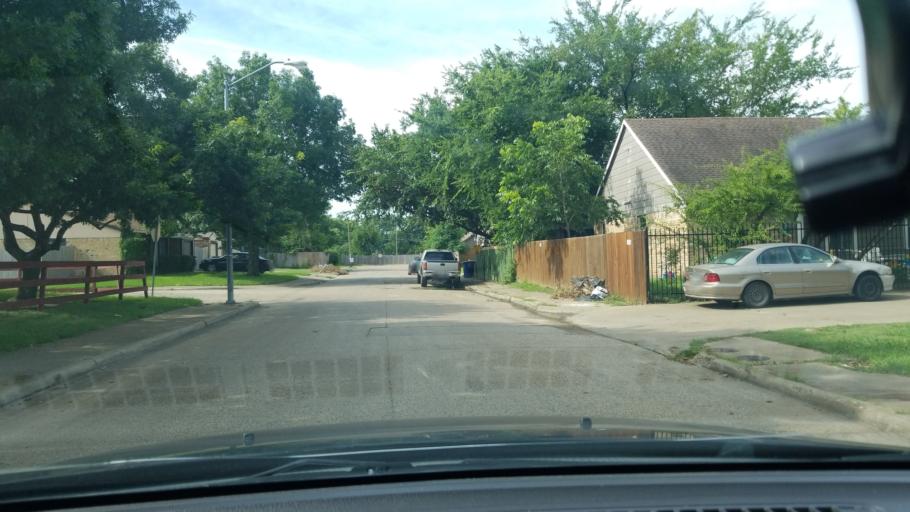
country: US
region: Texas
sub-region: Dallas County
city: Balch Springs
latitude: 32.7648
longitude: -96.6606
